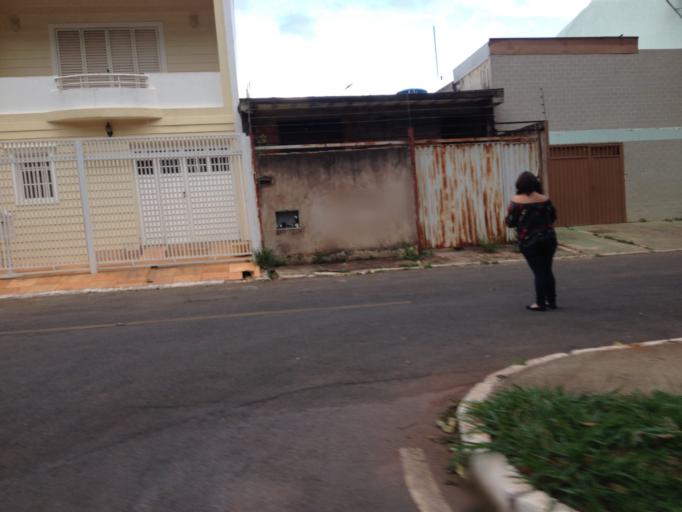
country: BR
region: Federal District
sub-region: Brasilia
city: Brasilia
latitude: -15.7822
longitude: -47.9368
